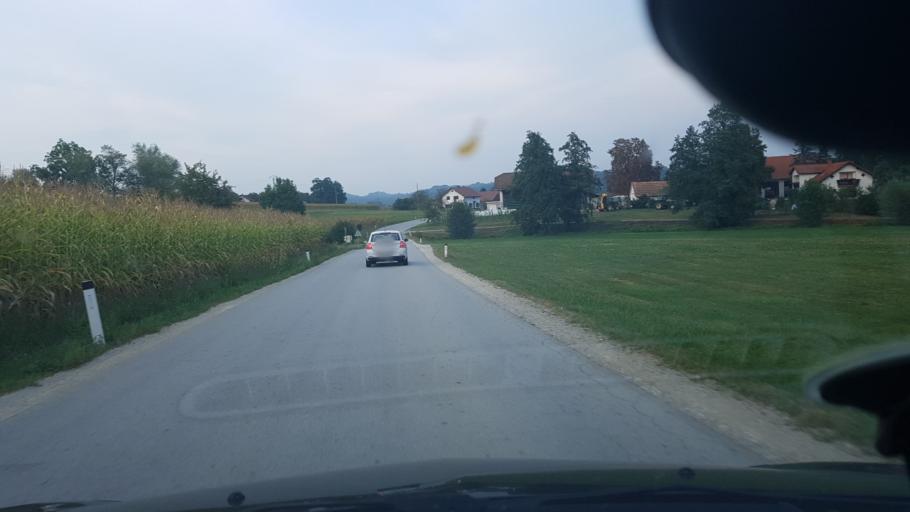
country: SI
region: Podcetrtek
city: Podcetrtek
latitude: 46.1088
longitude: 15.5989
